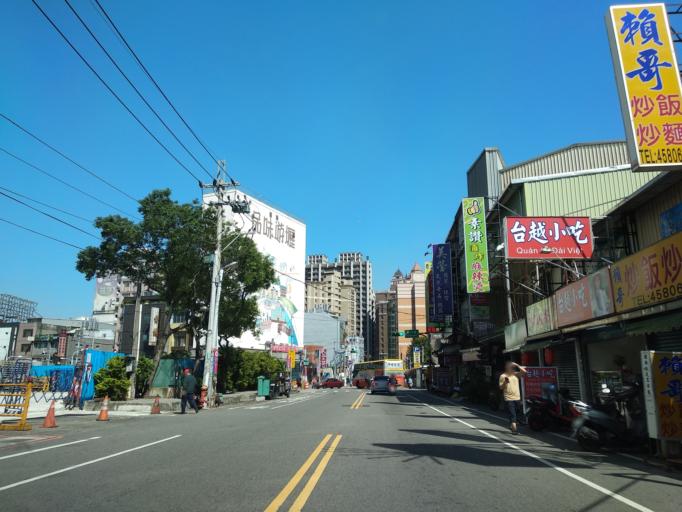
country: TW
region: Taiwan
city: Taoyuan City
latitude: 24.9515
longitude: 121.2261
